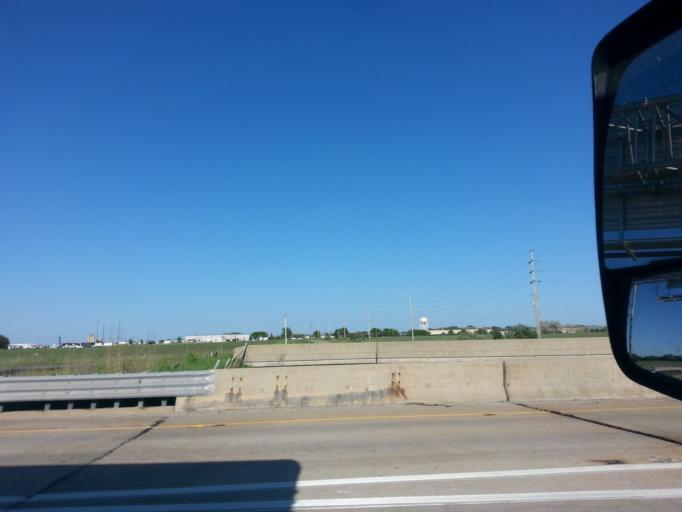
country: US
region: Illinois
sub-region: McLean County
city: Normal
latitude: 40.5469
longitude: -89.0032
